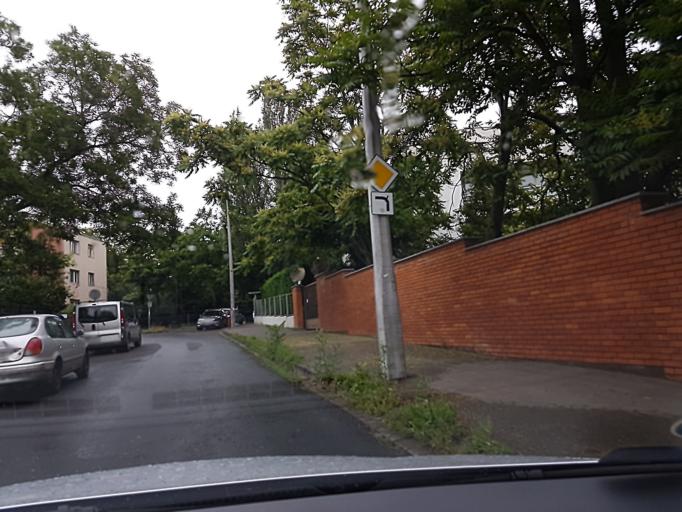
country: HU
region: Budapest
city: Budapest II. keruelet
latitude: 47.5213
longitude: 19.0251
